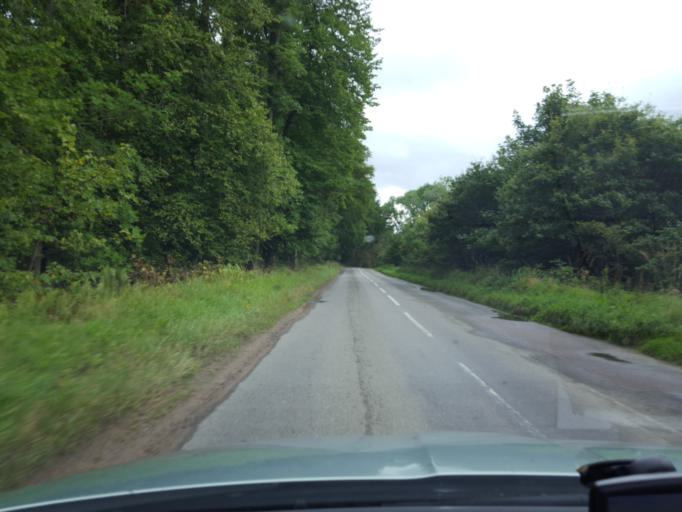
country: GB
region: Scotland
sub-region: Aberdeenshire
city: Kemnay
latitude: 57.1574
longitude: -2.4307
